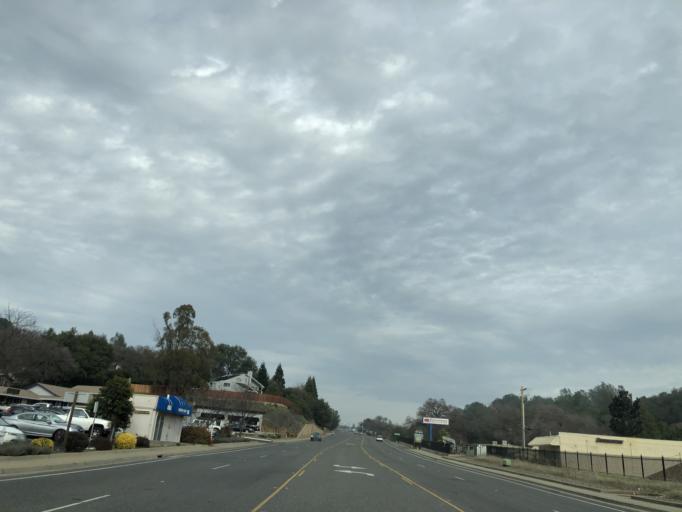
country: US
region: California
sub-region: El Dorado County
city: El Dorado Hills
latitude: 38.7026
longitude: -121.1043
